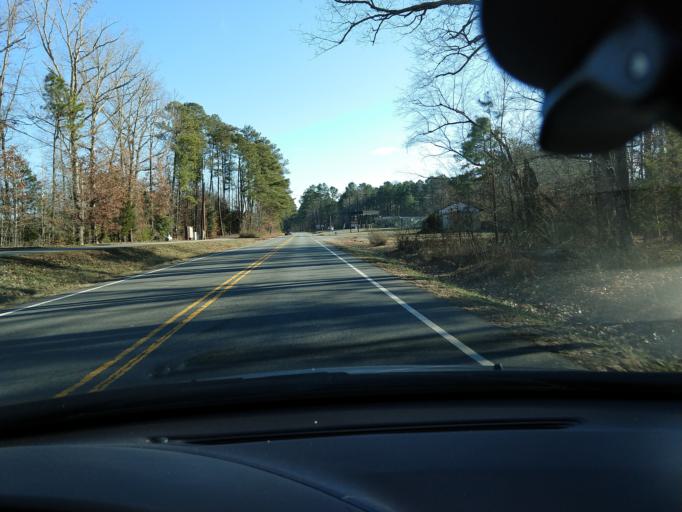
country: US
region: Virginia
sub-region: Charles City County
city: Charles City
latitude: 37.3117
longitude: -76.9650
